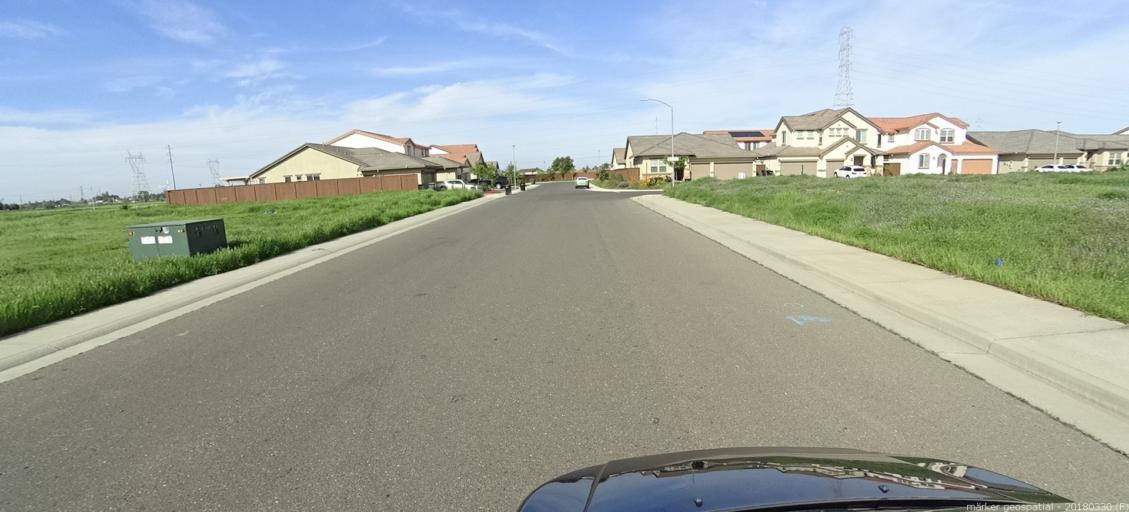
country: US
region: California
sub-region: Sacramento County
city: Vineyard
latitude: 38.4873
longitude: -121.3482
